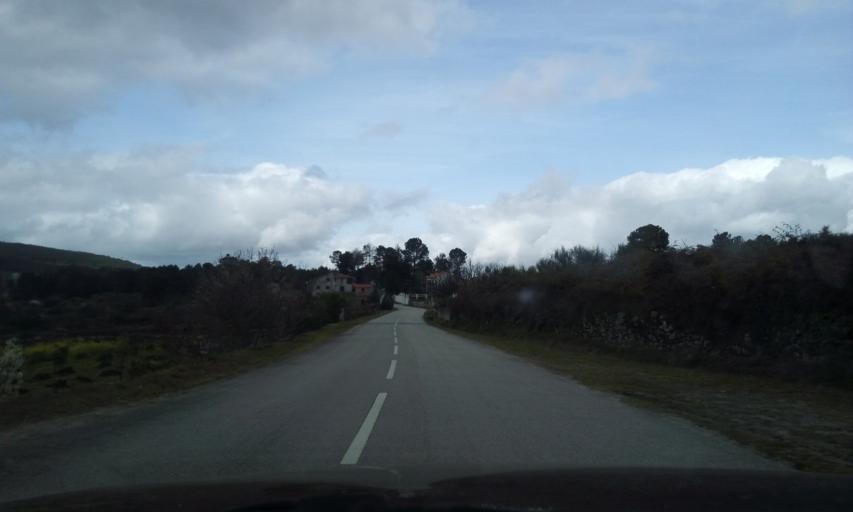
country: PT
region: Guarda
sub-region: Fornos de Algodres
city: Fornos de Algodres
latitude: 40.6605
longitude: -7.5964
